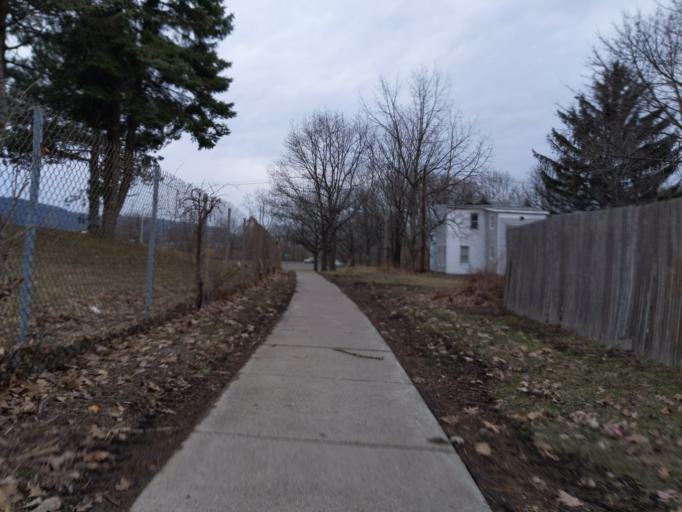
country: US
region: New York
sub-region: Chemung County
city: Elmira Heights
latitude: 42.1107
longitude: -76.8132
